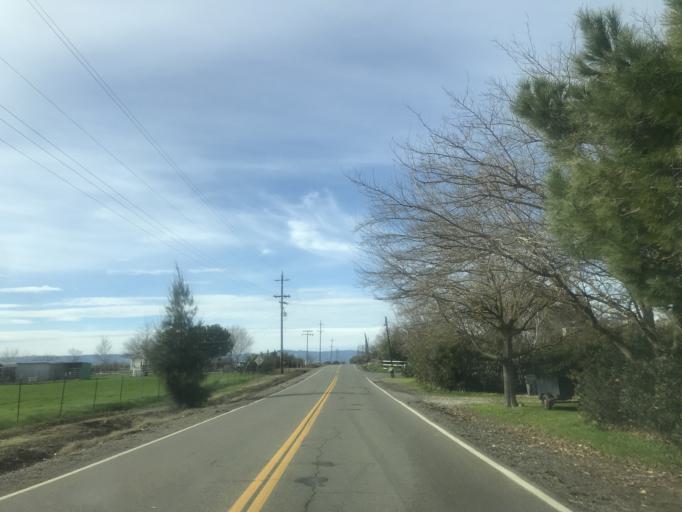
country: US
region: California
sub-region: Yolo County
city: Woodland
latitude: 38.6635
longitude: -121.8702
